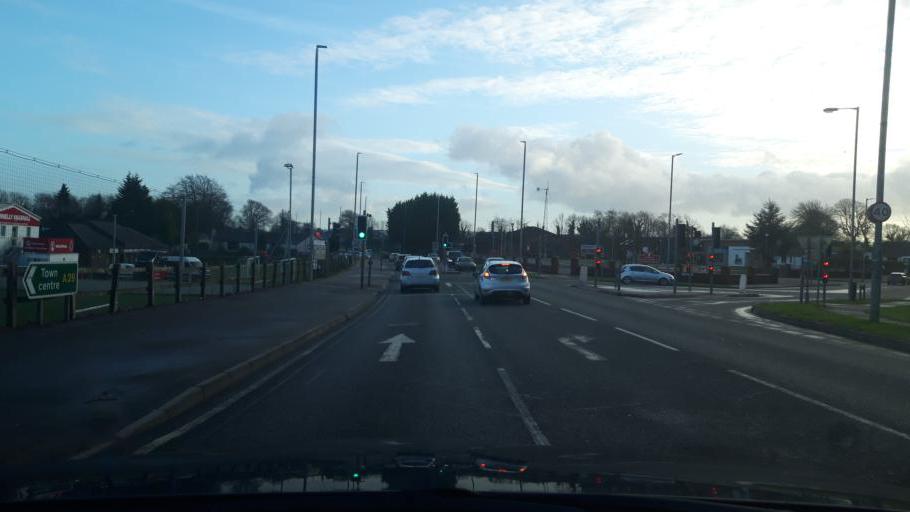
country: GB
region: Northern Ireland
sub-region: Dungannon District
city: Dungannon
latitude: 54.4894
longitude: -6.7479
